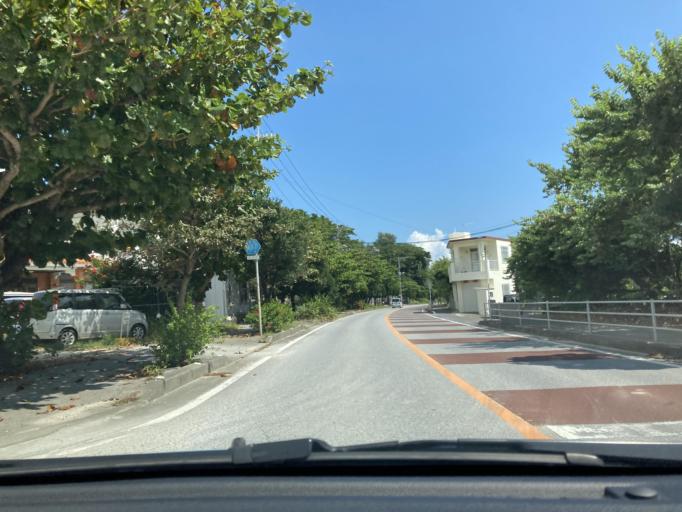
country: JP
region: Okinawa
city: Ginowan
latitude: 26.1810
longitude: 127.7694
